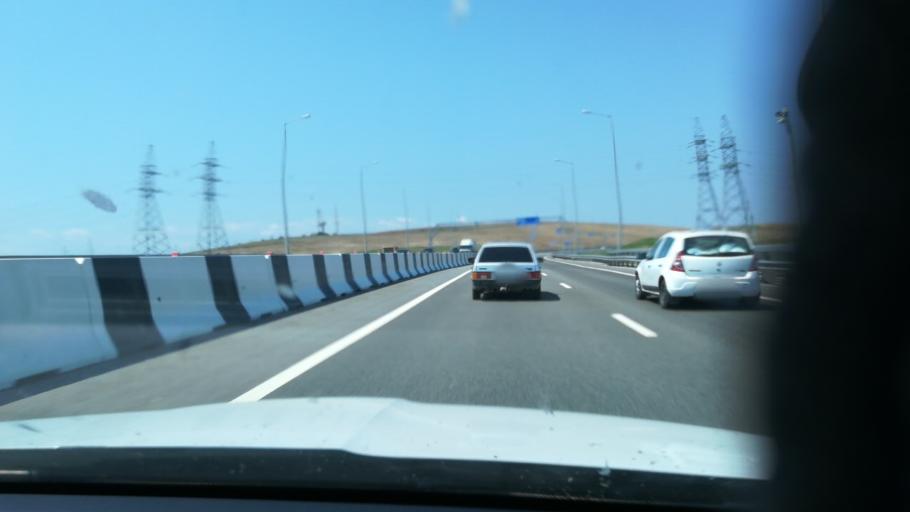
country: RU
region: Krasnodarskiy
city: Vyshestebliyevskaya
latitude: 45.2268
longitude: 37.0012
